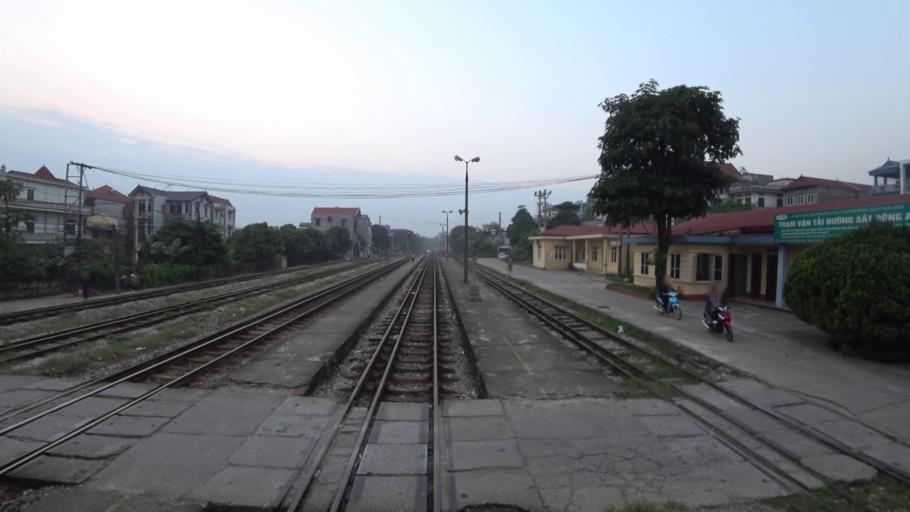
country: VN
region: Ha Noi
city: Dong Anh
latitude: 21.1844
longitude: 105.8543
